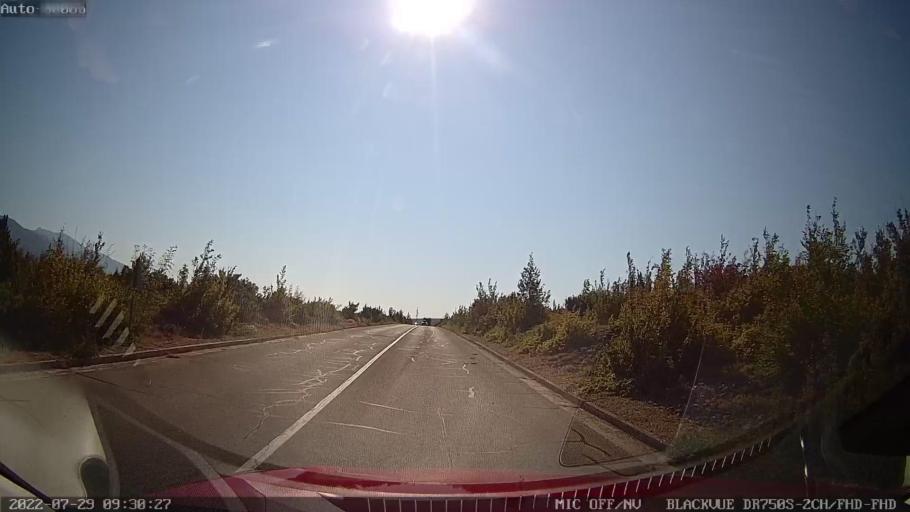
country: HR
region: Zadarska
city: Obrovac
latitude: 44.1937
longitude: 15.6863
